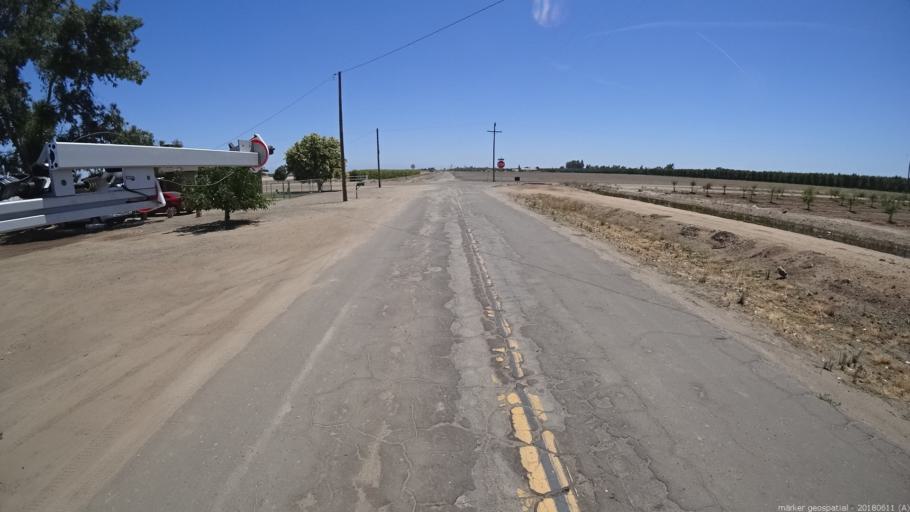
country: US
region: California
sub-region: Madera County
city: Fairmead
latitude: 37.0256
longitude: -120.2030
